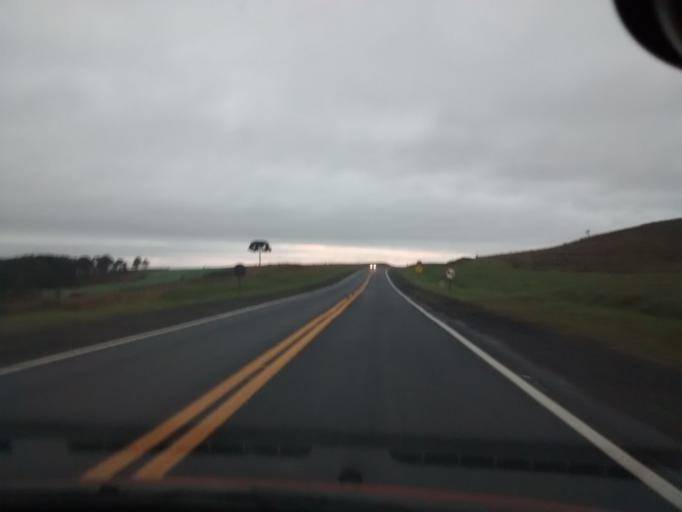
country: BR
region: Rio Grande do Sul
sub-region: Vacaria
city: Estrela
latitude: -28.1698
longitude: -50.6718
